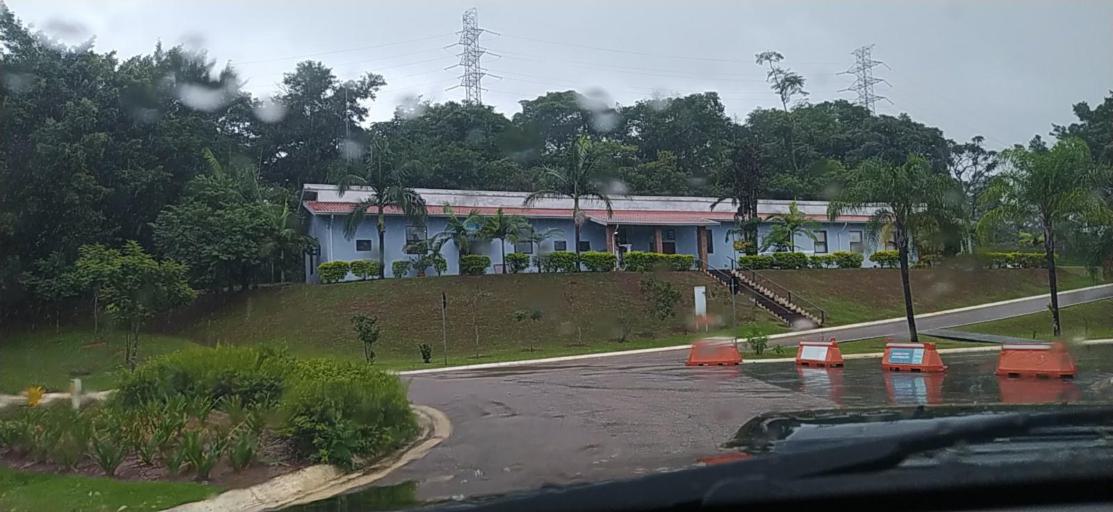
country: BR
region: Sao Paulo
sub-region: Jundiai
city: Jundiai
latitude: -23.1549
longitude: -46.8917
